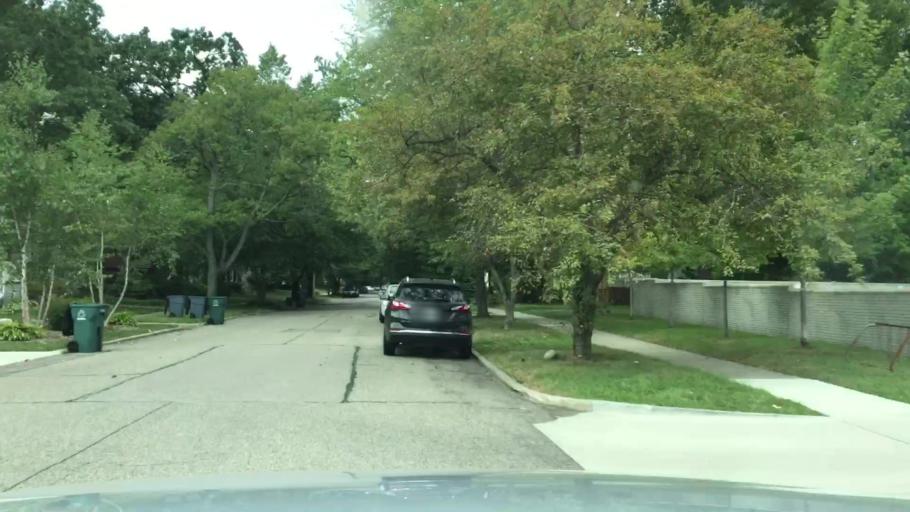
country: US
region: Michigan
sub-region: Oakland County
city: Ferndale
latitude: 42.4644
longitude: -83.1379
